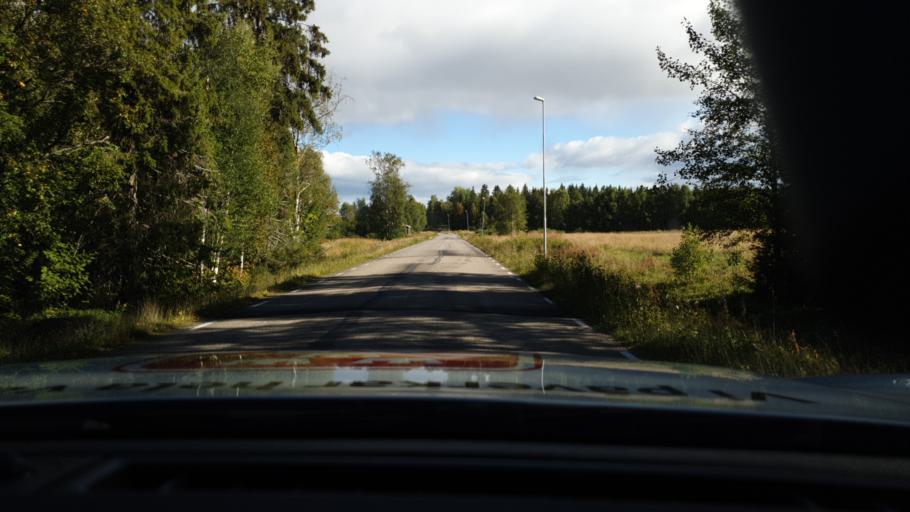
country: SE
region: Norrbotten
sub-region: Pajala Kommun
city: Pajala
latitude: 67.1618
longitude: 22.6191
